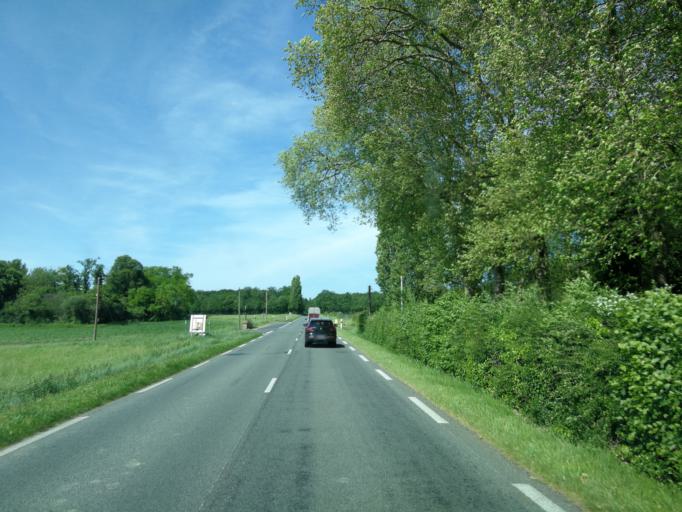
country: FR
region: Centre
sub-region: Departement d'Indre-et-Loire
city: Ligre
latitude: 47.0935
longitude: 0.1852
